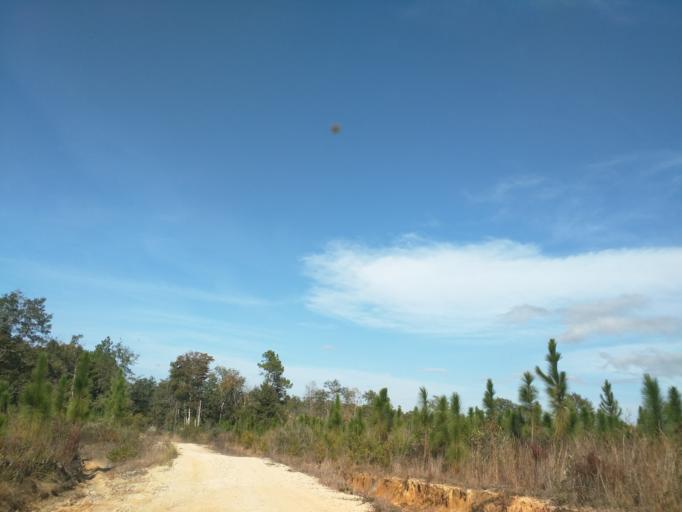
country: US
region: Florida
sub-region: Escambia County
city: Cantonment
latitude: 30.5393
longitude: -87.4309
